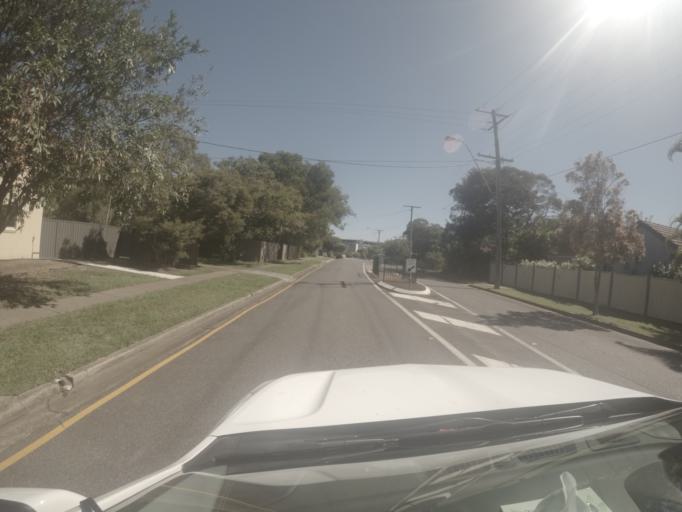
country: AU
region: Queensland
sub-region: Brisbane
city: Rocklea
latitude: -27.5349
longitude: 152.9850
